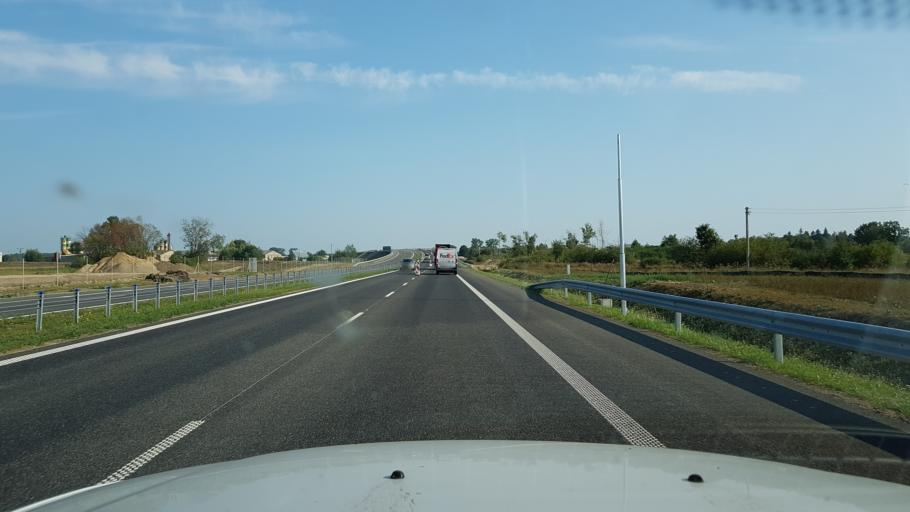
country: PL
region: West Pomeranian Voivodeship
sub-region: Powiat gryficki
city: Ploty
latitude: 53.7920
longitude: 15.2522
